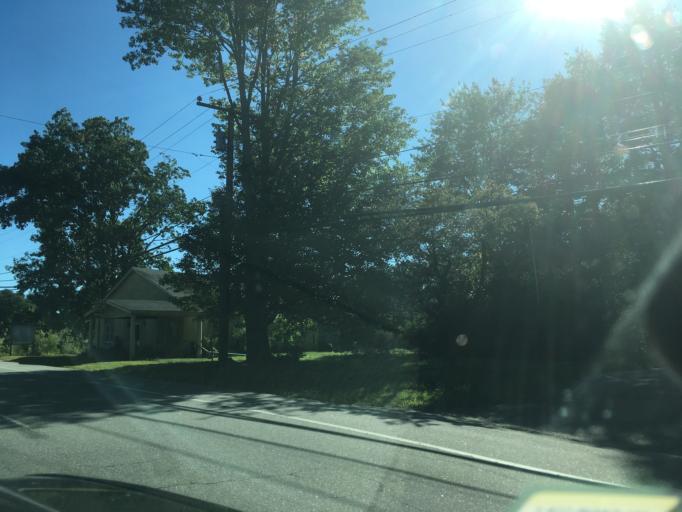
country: US
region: New Hampshire
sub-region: Rockingham County
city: Stratham Station
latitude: 43.0224
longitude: -70.9174
